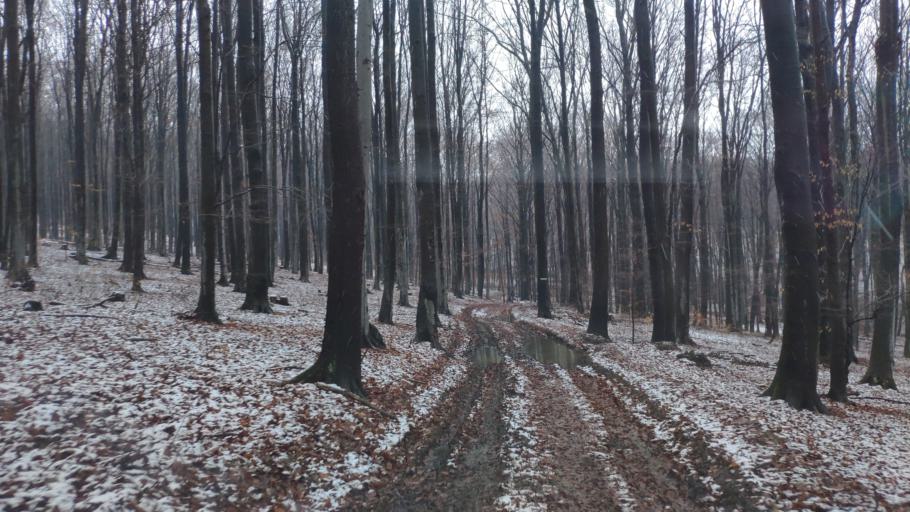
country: SK
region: Kosicky
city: Moldava nad Bodvou
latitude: 48.7368
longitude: 21.0681
